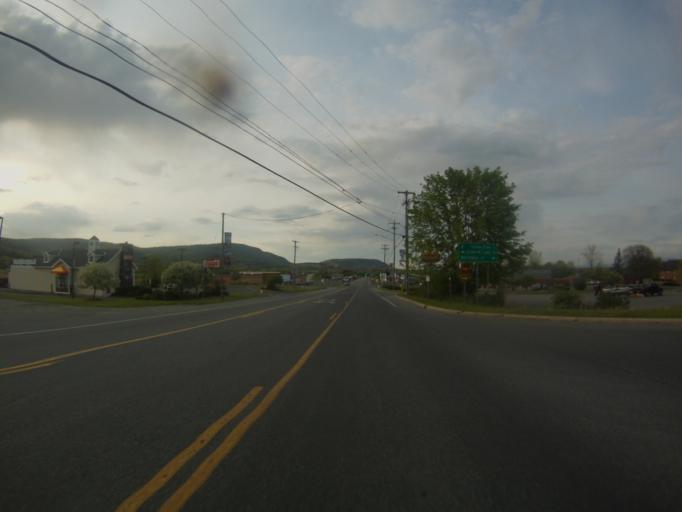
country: US
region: New York
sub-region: Essex County
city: Ticonderoga
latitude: 43.8572
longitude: -73.4381
